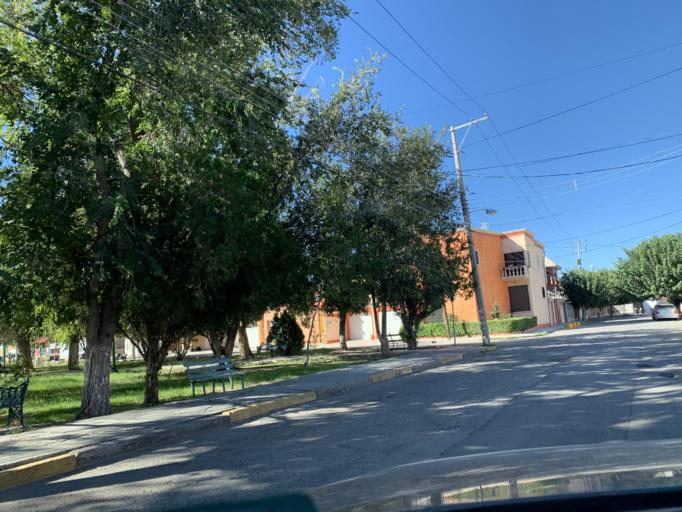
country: MX
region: Chihuahua
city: Ciudad Juarez
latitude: 31.7402
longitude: -106.4445
